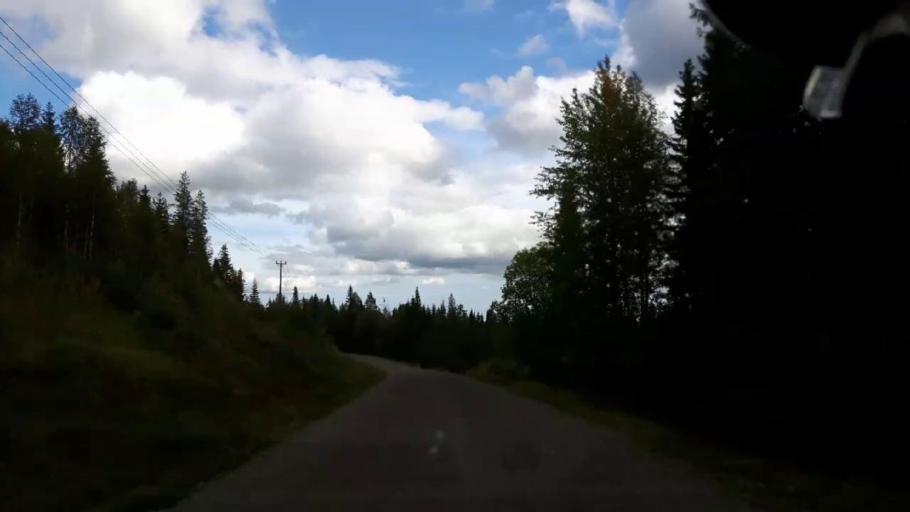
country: SE
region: Jaemtland
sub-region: Stroemsunds Kommun
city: Stroemsund
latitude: 63.4173
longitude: 15.8537
